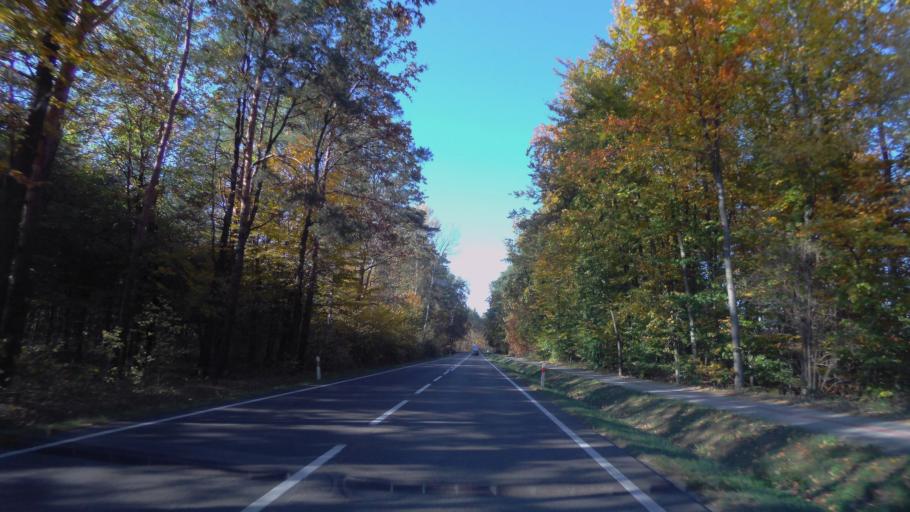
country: PL
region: Subcarpathian Voivodeship
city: Nowa Sarzyna
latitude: 50.2965
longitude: 22.3722
